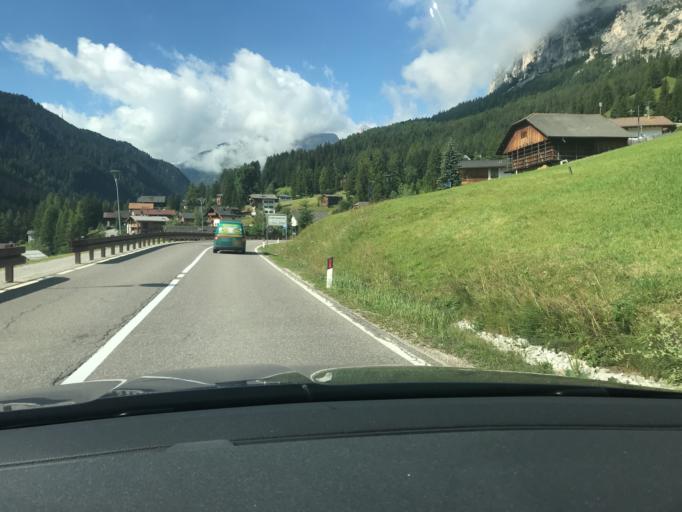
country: IT
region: Trentino-Alto Adige
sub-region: Bolzano
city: Badia
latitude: 46.5774
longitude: 11.8948
